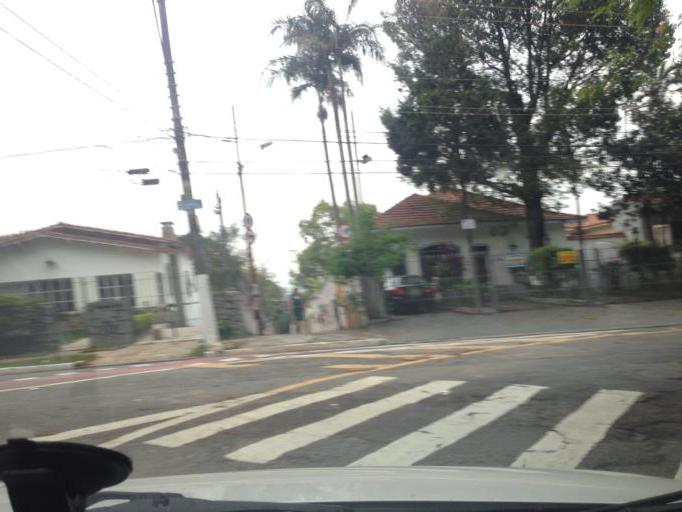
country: BR
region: Sao Paulo
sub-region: Osasco
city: Osasco
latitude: -23.5278
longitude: -46.7158
